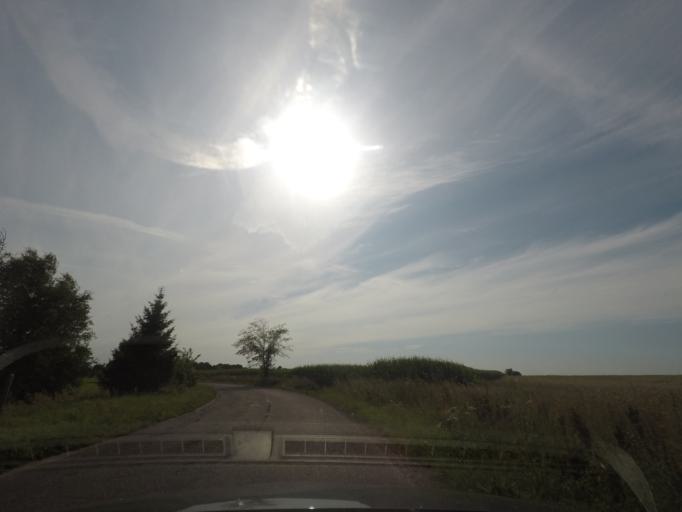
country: PL
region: Pomeranian Voivodeship
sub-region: Powiat slupski
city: Smoldzino
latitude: 54.6299
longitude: 17.2470
